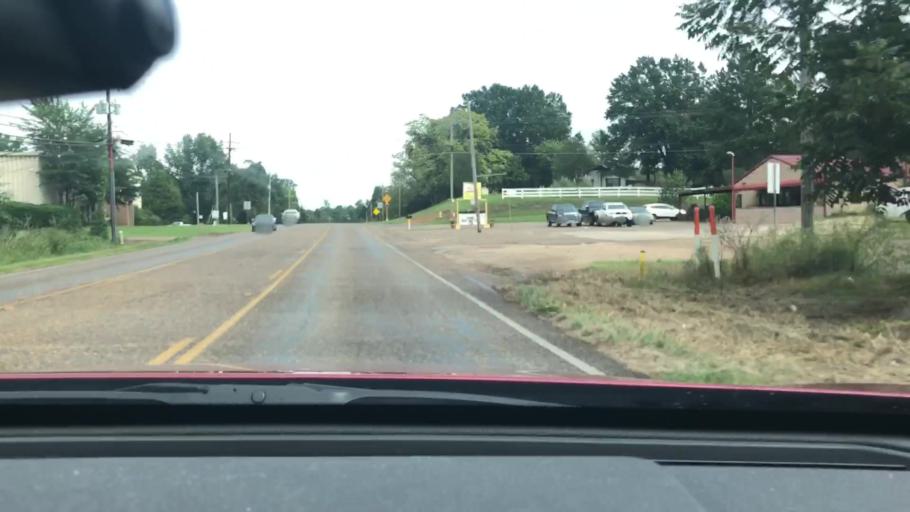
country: US
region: Texas
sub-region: Bowie County
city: Wake Village
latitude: 33.4429
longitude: -94.1118
